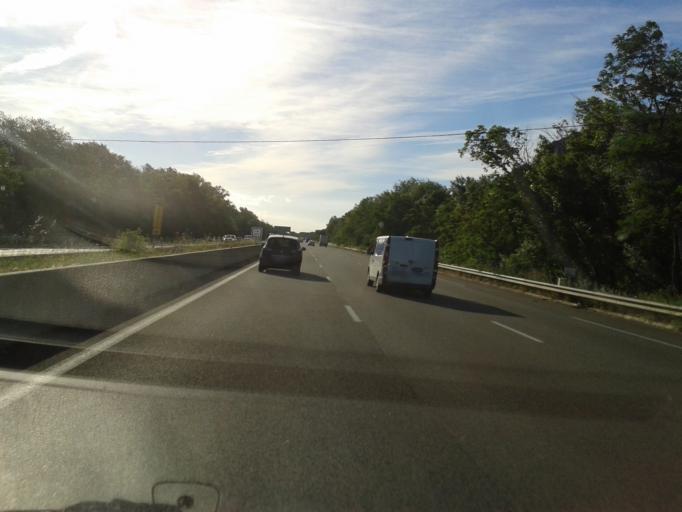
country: FR
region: Provence-Alpes-Cote d'Azur
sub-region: Departement du Var
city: Le Muy
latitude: 43.4628
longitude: 6.5838
